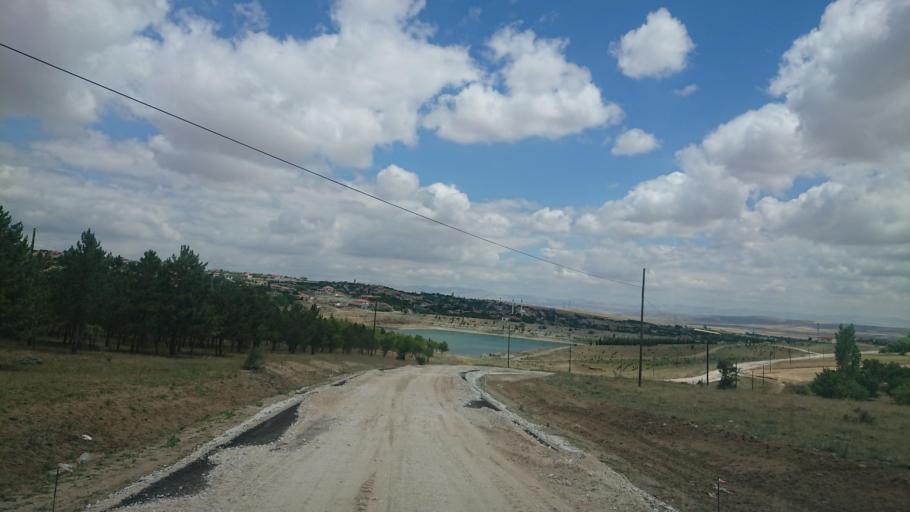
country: TR
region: Aksaray
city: Agacoren
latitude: 38.8602
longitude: 33.9478
